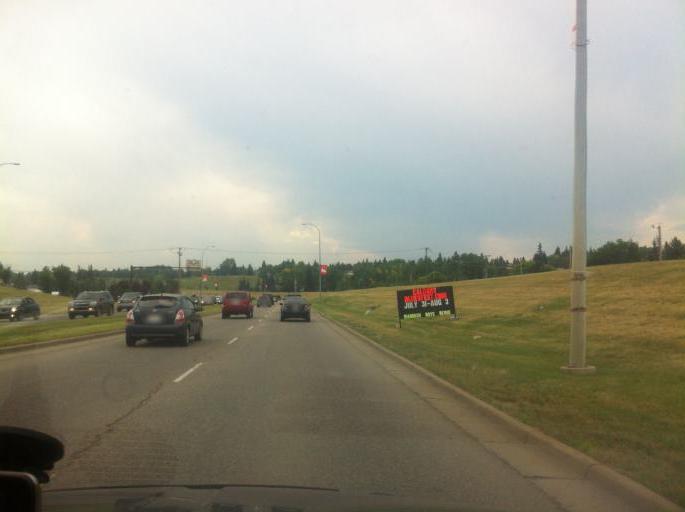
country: CA
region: Alberta
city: Calgary
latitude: 50.9411
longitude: -114.0294
